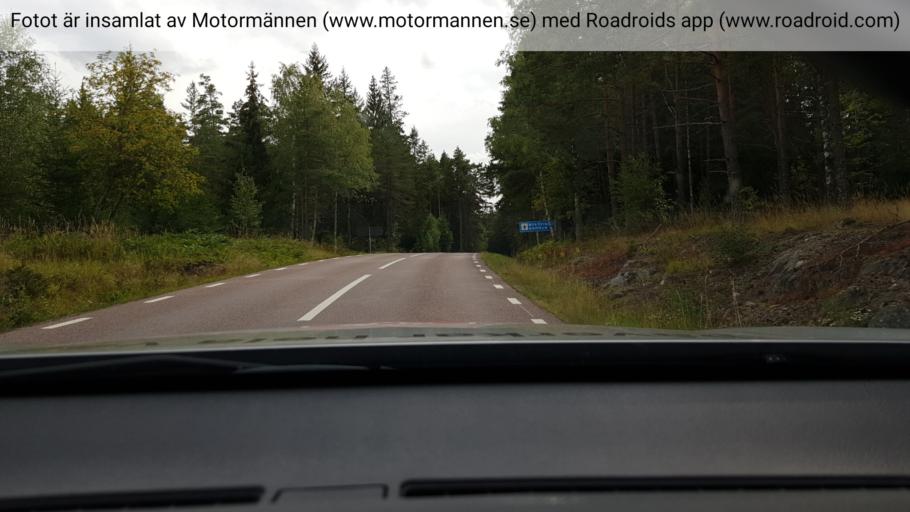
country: SE
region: Soedermanland
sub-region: Gnesta Kommun
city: Gnesta
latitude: 58.9777
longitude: 17.1516
